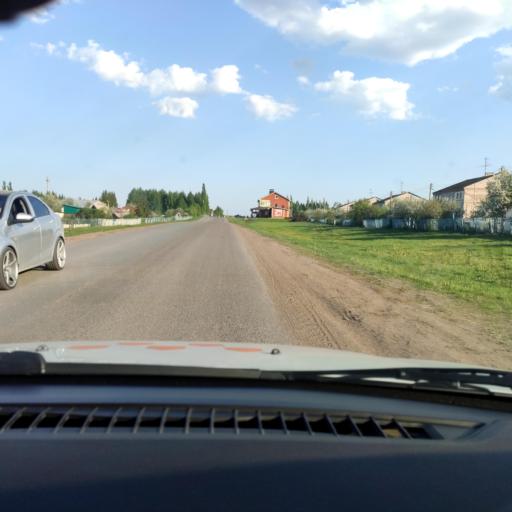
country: RU
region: Bashkortostan
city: Karmaskaly
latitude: 54.3698
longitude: 56.1548
